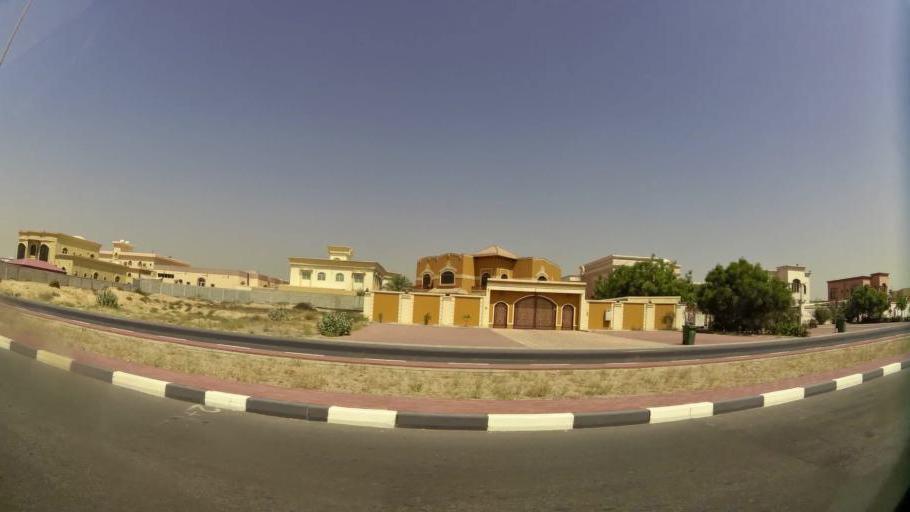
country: AE
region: Ajman
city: Ajman
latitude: 25.4209
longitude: 55.5289
